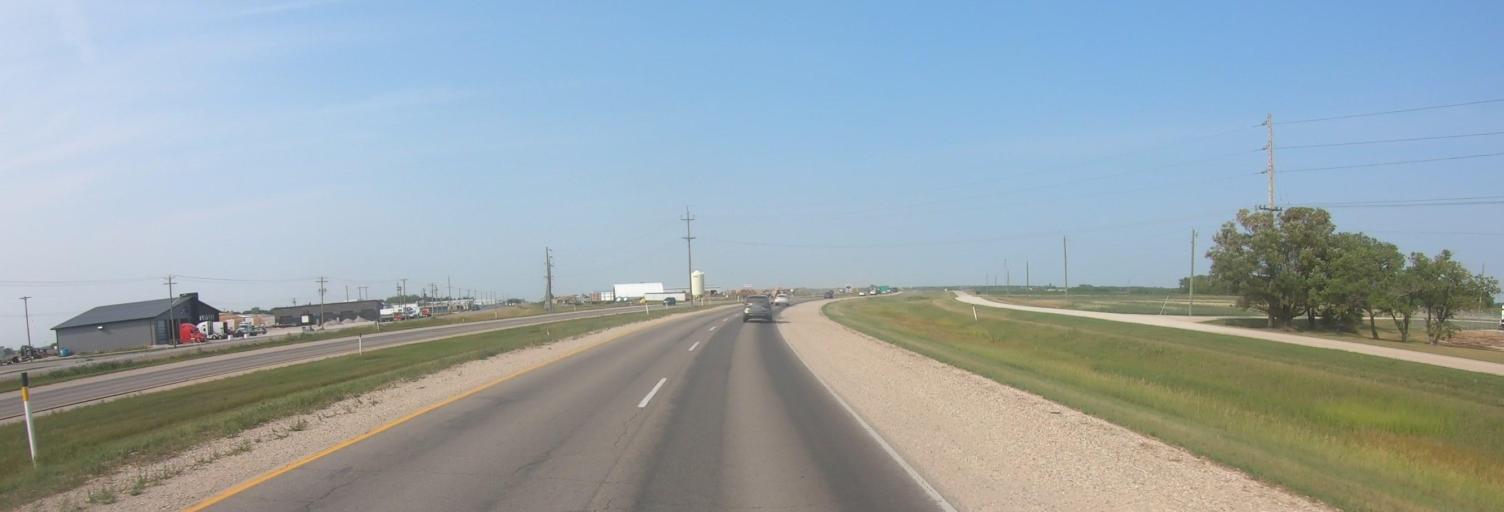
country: CA
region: Manitoba
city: Steinbach
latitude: 49.5966
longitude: -96.6867
